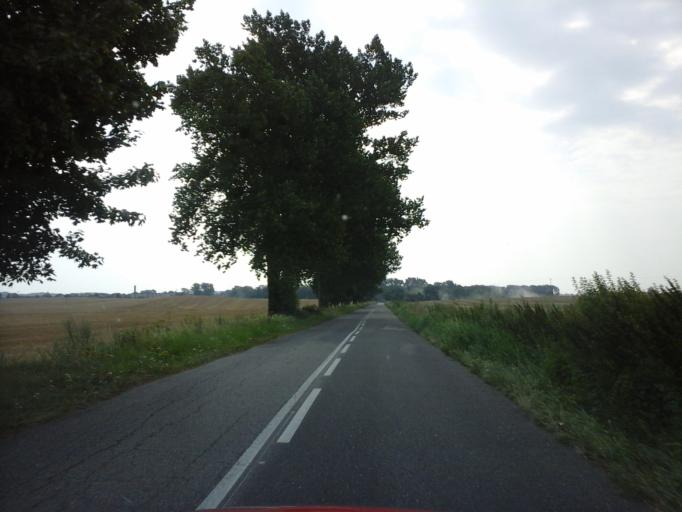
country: PL
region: West Pomeranian Voivodeship
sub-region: Powiat choszczenski
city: Pelczyce
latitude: 53.0536
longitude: 15.3676
